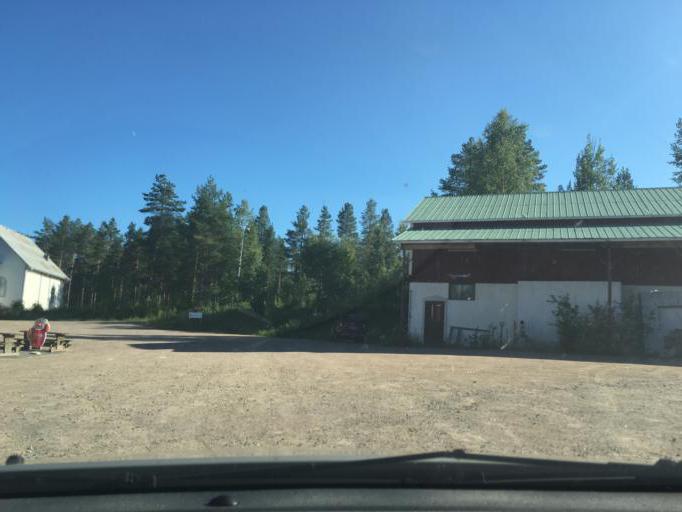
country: SE
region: Norrbotten
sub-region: Kalix Kommun
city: Toere
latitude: 66.0680
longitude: 22.6992
